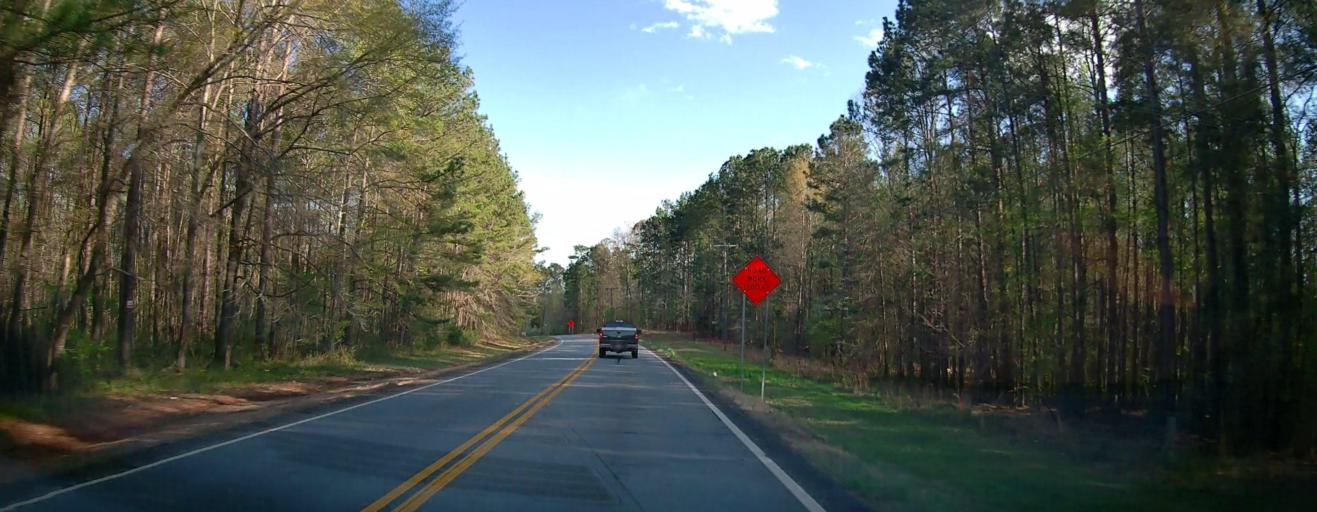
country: US
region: Georgia
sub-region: Putnam County
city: Eatonton
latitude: 33.1850
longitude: -83.4138
